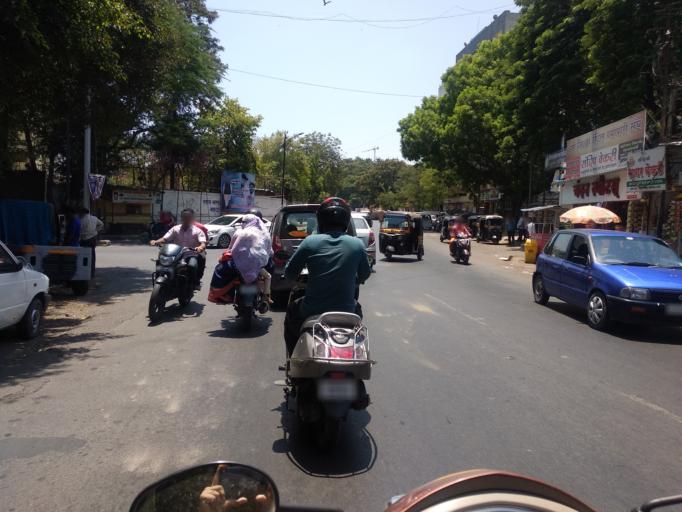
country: IN
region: Maharashtra
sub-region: Pune Division
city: Pune
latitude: 18.5041
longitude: 73.8472
